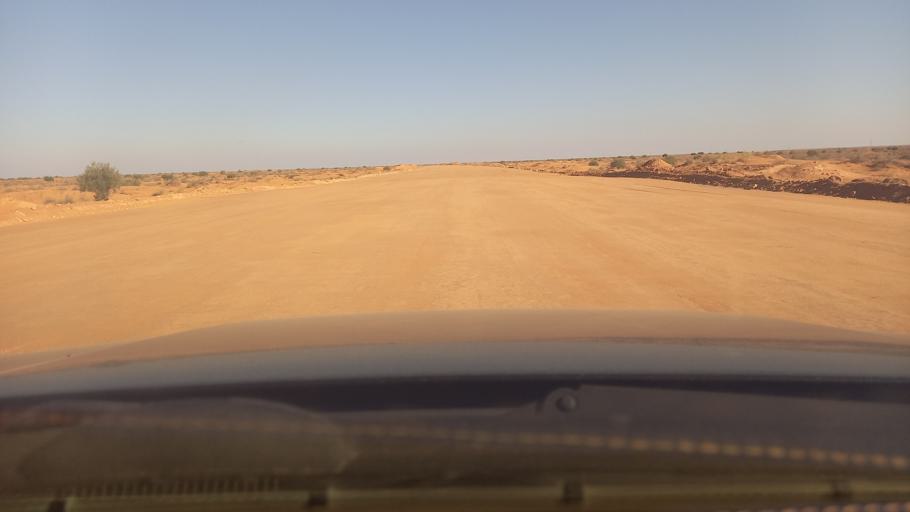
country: TN
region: Madanin
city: Medenine
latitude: 33.1573
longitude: 10.5154
